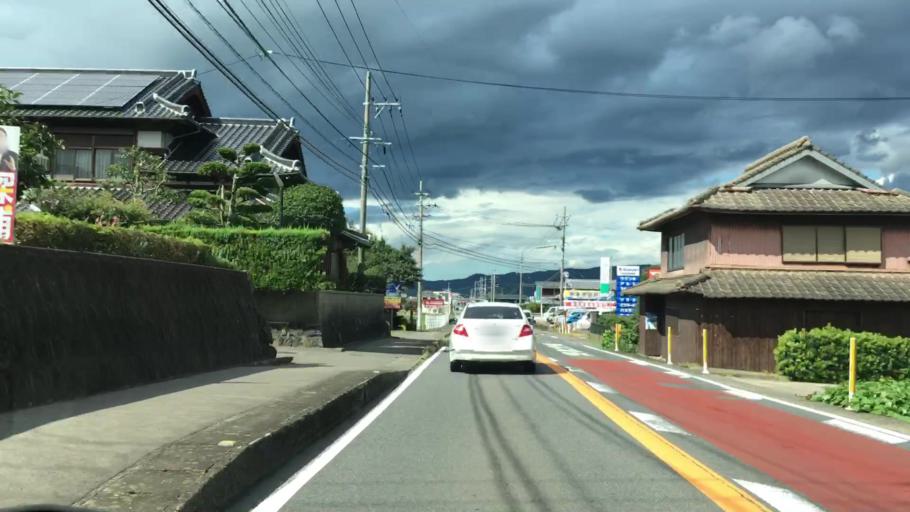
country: JP
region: Saga Prefecture
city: Imaricho-ko
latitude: 33.2459
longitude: 129.8515
